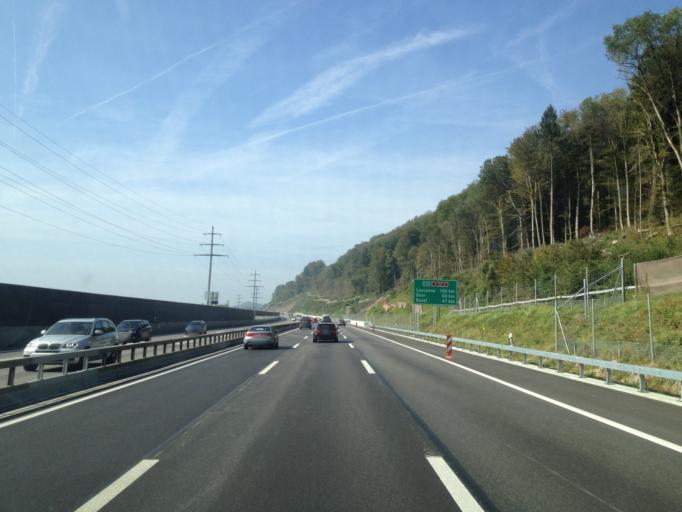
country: CH
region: Aargau
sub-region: Bezirk Zofingen
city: Rothrist
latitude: 47.3133
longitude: 7.8812
